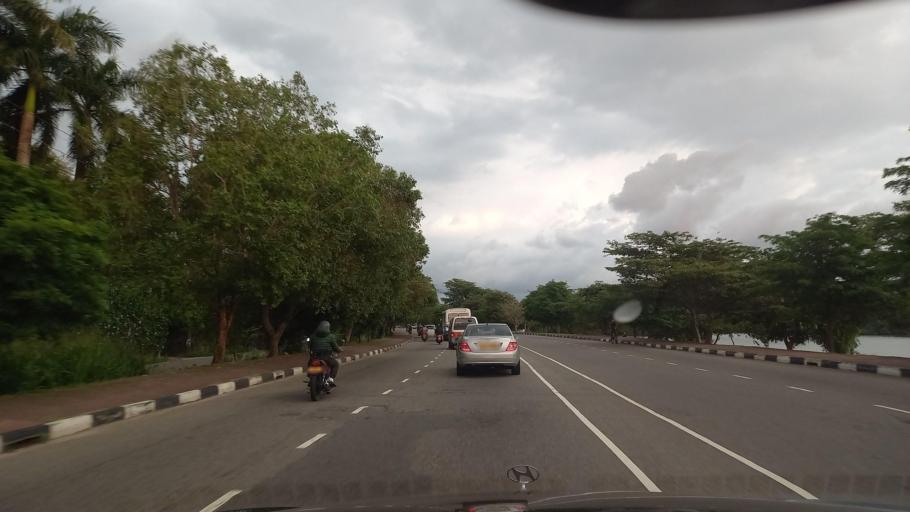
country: LK
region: Western
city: Battaramulla South
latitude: 6.8858
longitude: 79.9239
